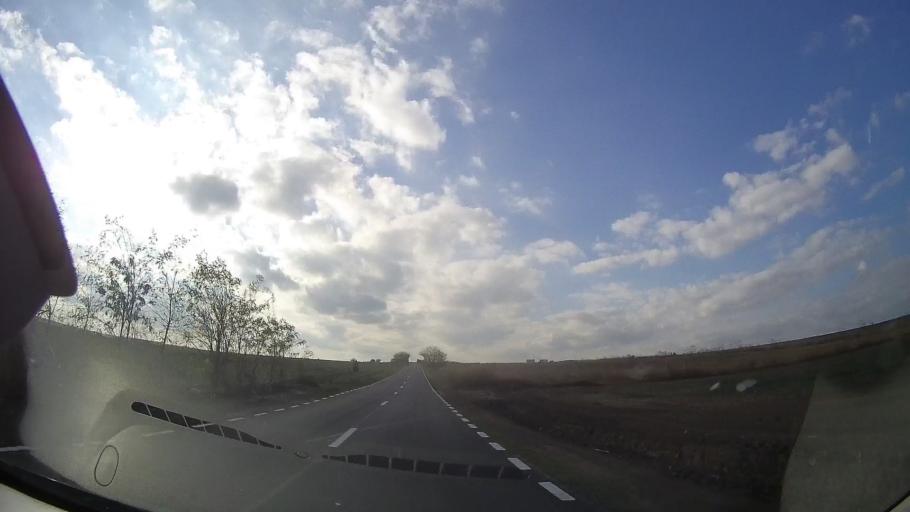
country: RO
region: Constanta
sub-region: Comuna Limanu
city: Limanu
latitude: 43.8235
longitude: 28.4852
